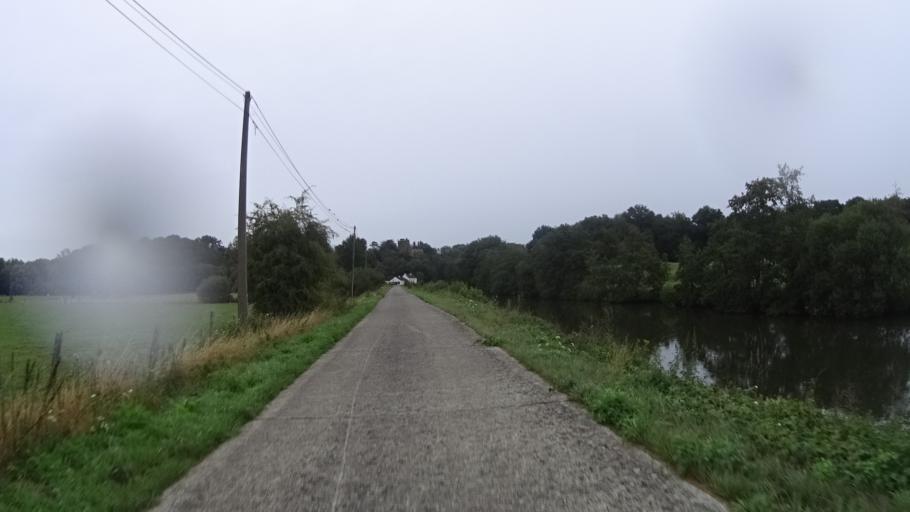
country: BE
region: Wallonia
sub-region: Province du Hainaut
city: Lobbes
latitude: 50.3296
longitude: 4.2304
